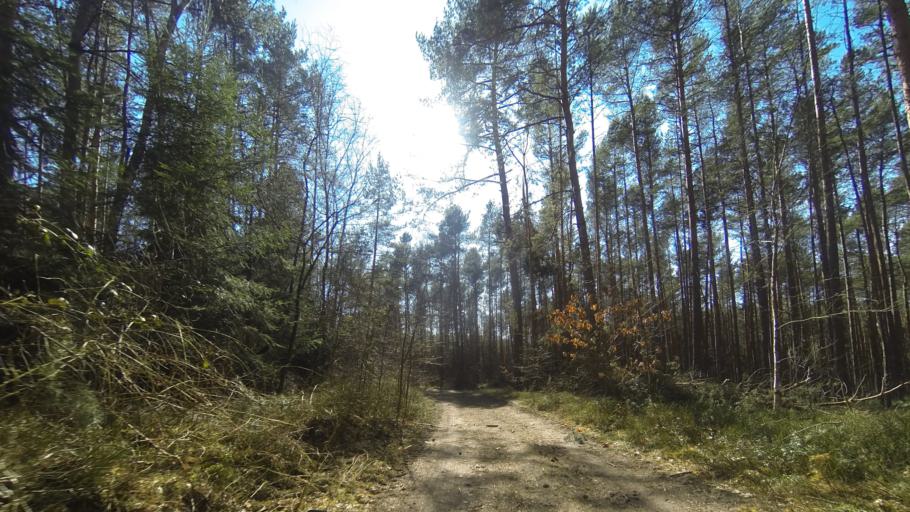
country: DE
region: Saxony
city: Ottendorf-Okrilla
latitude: 51.2003
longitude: 13.8003
